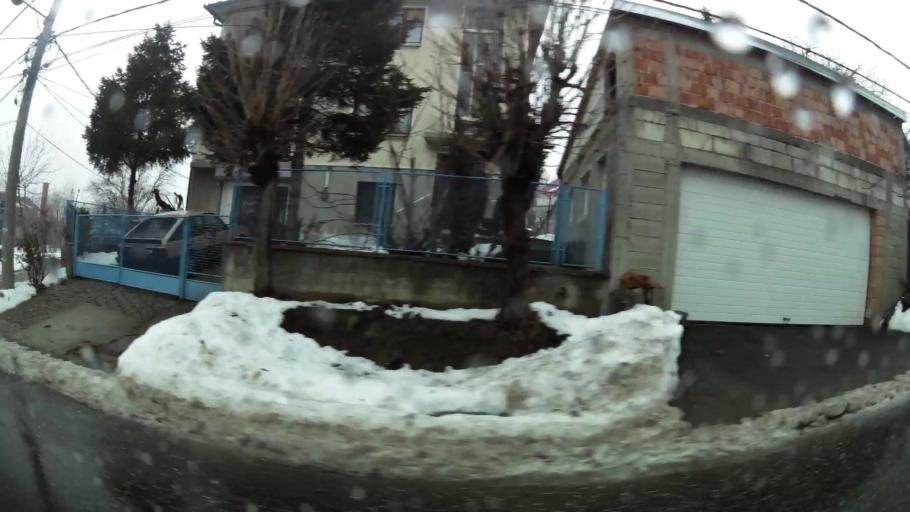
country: RS
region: Central Serbia
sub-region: Belgrade
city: Zvezdara
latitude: 44.7742
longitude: 20.5290
